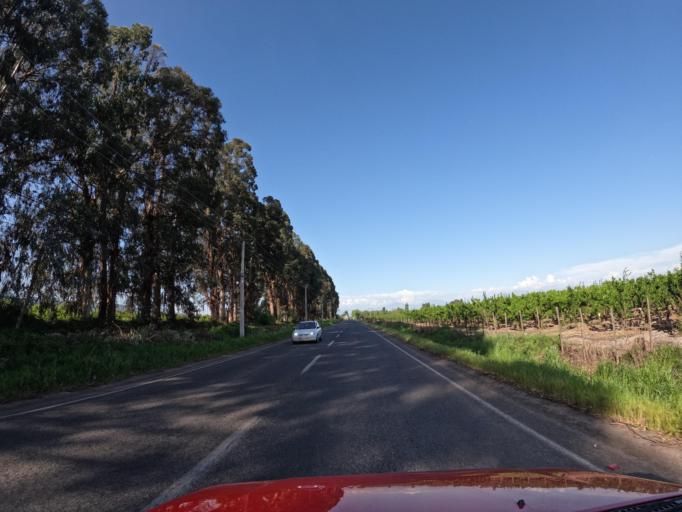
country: CL
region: Maule
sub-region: Provincia de Curico
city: Teno
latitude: -34.8660
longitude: -71.2071
